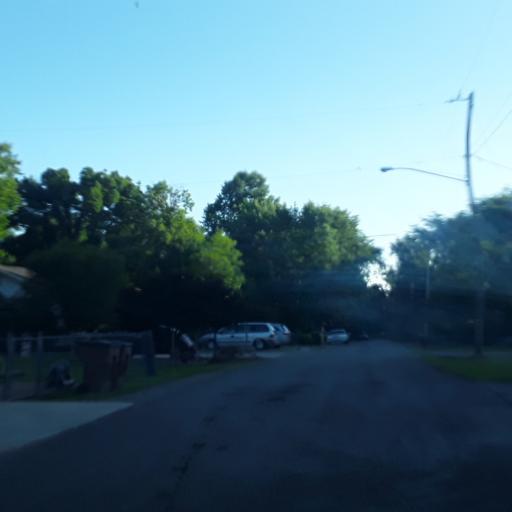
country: US
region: Tennessee
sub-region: Davidson County
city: Oak Hill
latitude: 36.1012
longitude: -86.7323
